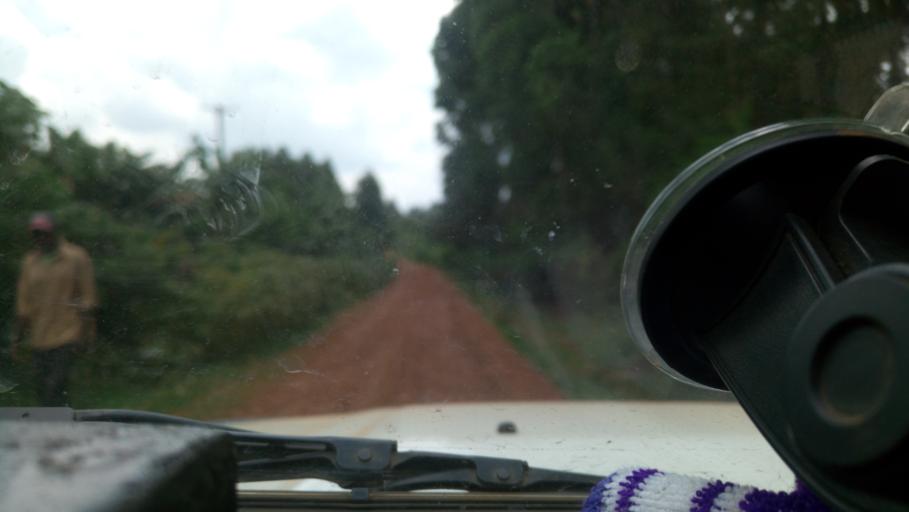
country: KE
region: Kericho
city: Litein
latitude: -0.5971
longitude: 35.1555
